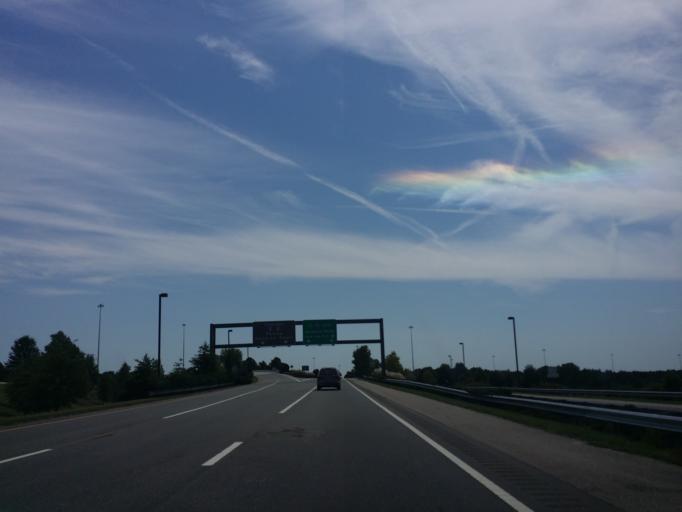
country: US
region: North Carolina
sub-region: Wake County
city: Morrisville
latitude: 35.8697
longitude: -78.8058
